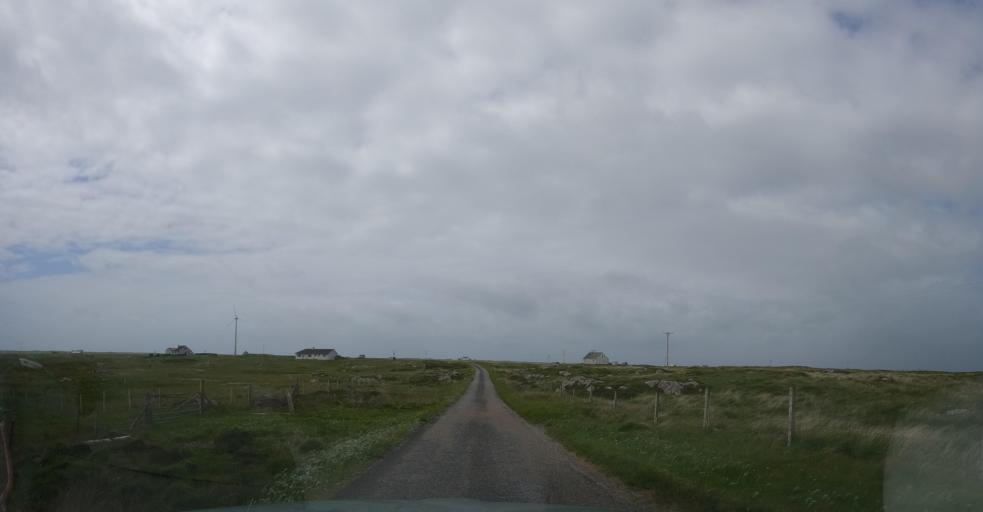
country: GB
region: Scotland
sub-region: Eilean Siar
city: Isle of South Uist
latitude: 57.2412
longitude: -7.3962
